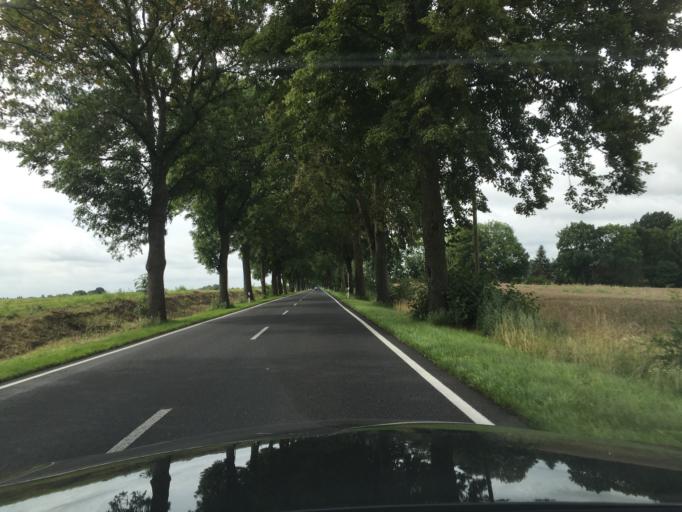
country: DE
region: Brandenburg
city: Gransee
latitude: 52.9090
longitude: 13.1585
